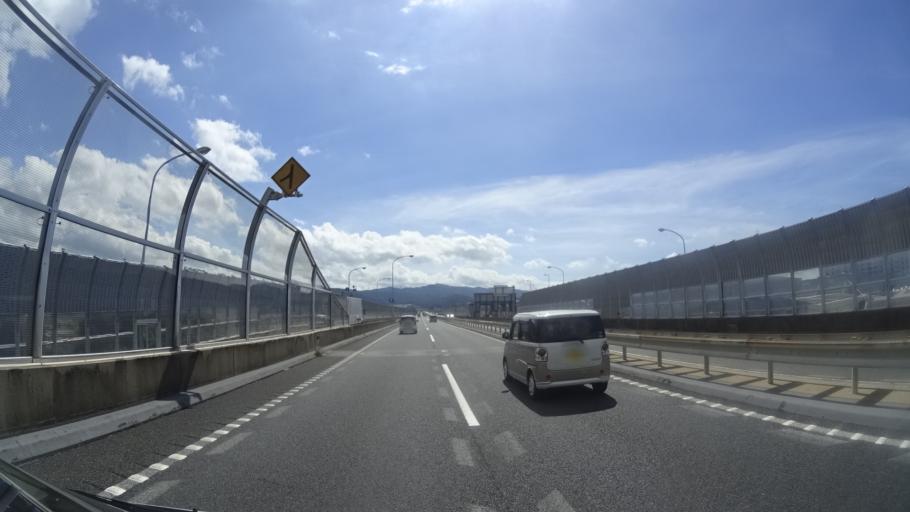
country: JP
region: Kyoto
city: Uji
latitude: 34.9071
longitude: 135.7870
